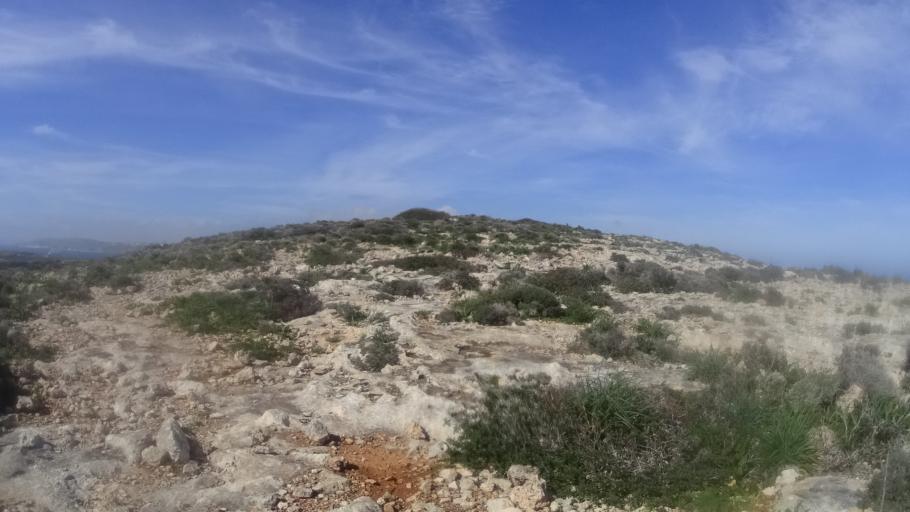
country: MT
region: Il-Qala
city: Qala
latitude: 36.0143
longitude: 14.3429
